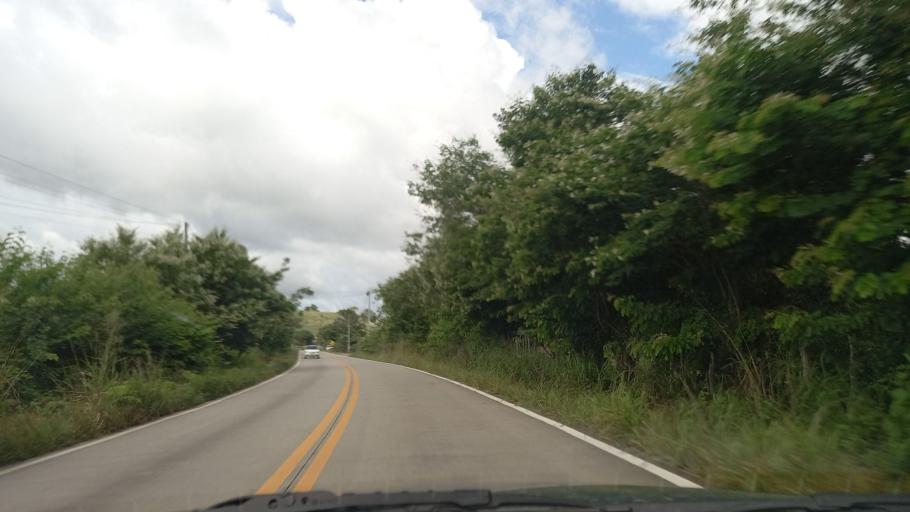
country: BR
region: Pernambuco
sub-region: Maraial
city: Maraial
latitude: -8.7916
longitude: -35.8893
